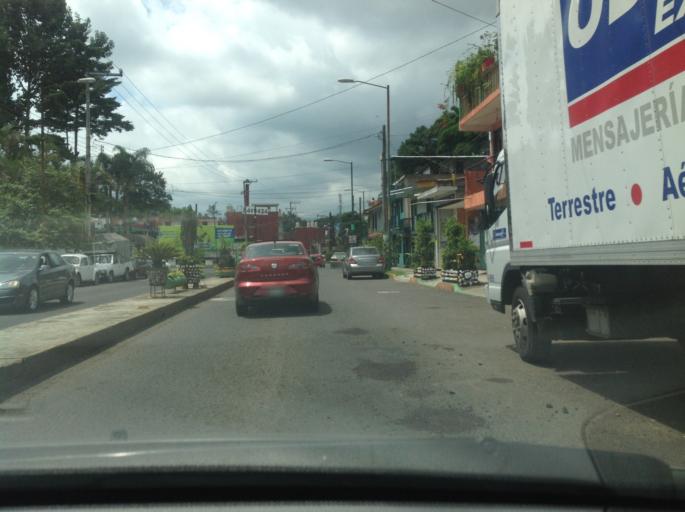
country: MX
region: Veracruz
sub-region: Xalapa
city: Xalapa de Enriquez
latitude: 19.5154
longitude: -96.9109
